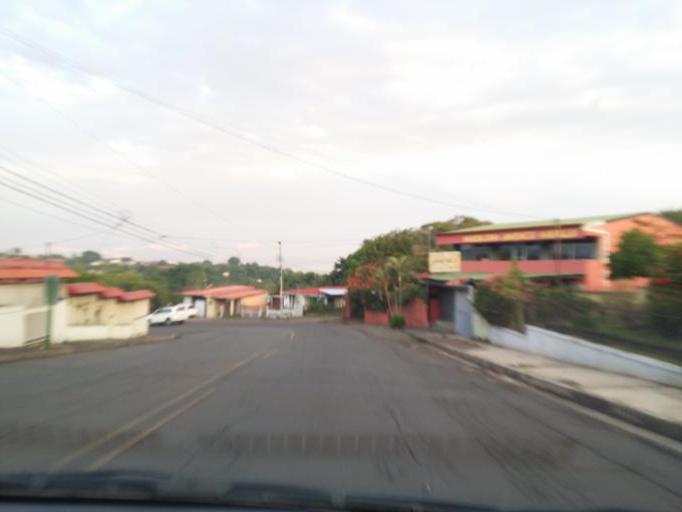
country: CR
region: Alajuela
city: San Juan
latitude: 10.0885
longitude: -84.3457
